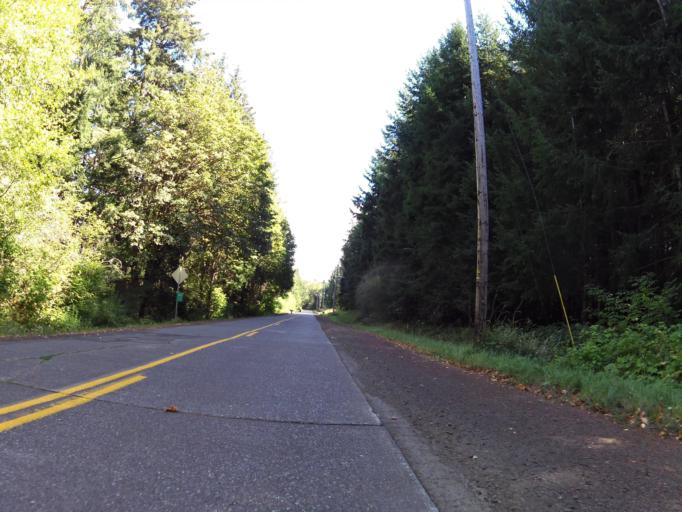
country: US
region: Washington
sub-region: Mason County
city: Shelton
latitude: 47.0946
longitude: -123.0898
